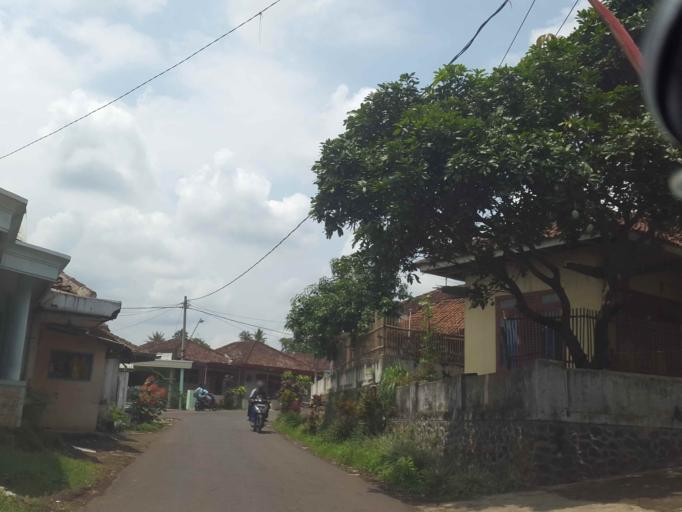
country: ID
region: East Java
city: Batu
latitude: -7.8712
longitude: 112.5902
